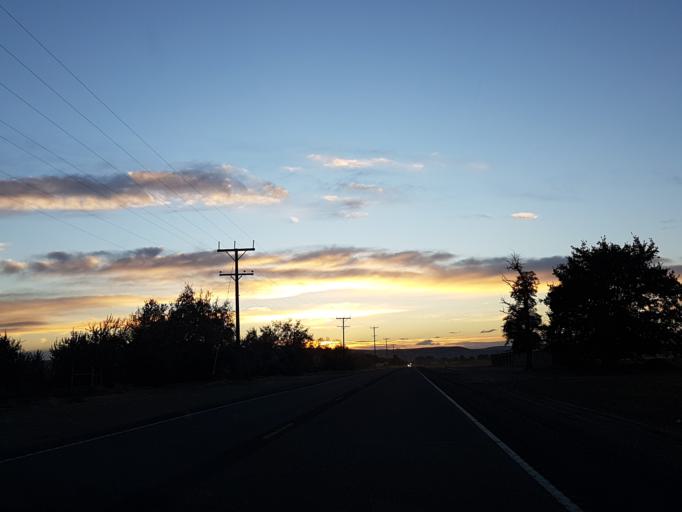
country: US
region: Oregon
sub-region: Malheur County
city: Vale
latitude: 43.9392
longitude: -117.3459
